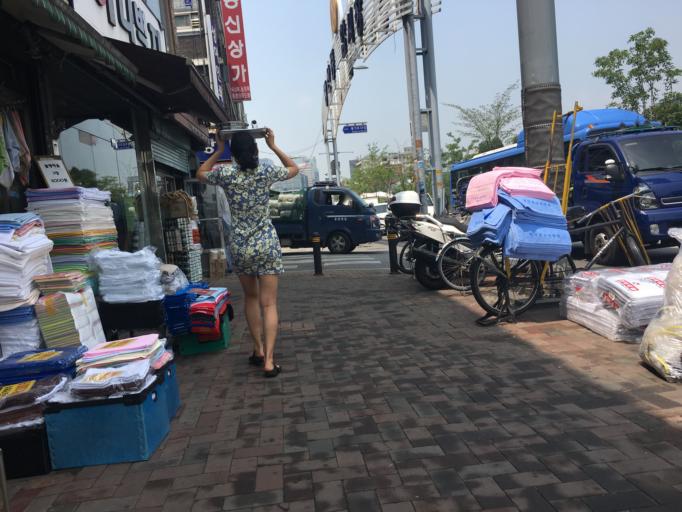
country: KR
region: Seoul
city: Seoul
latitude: 37.5697
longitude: 127.0016
